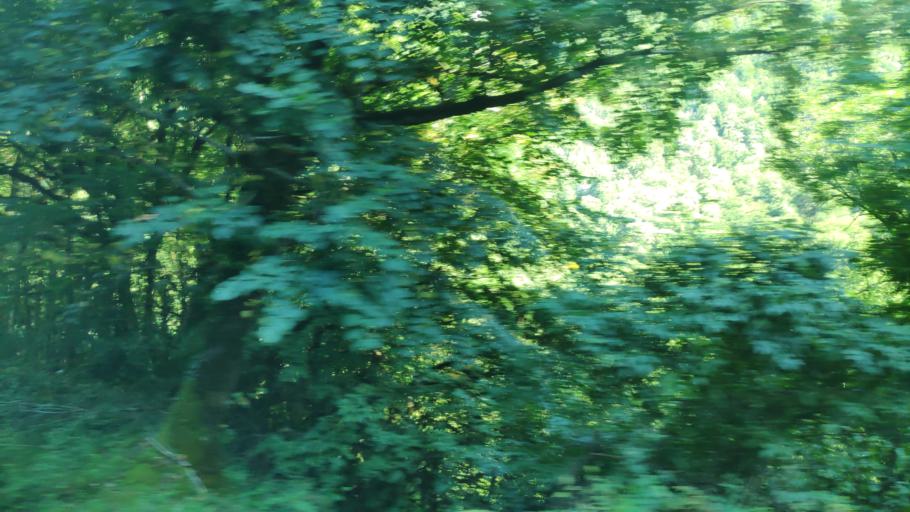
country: GE
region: Abkhazia
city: Gagra
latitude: 43.3549
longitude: 40.4214
